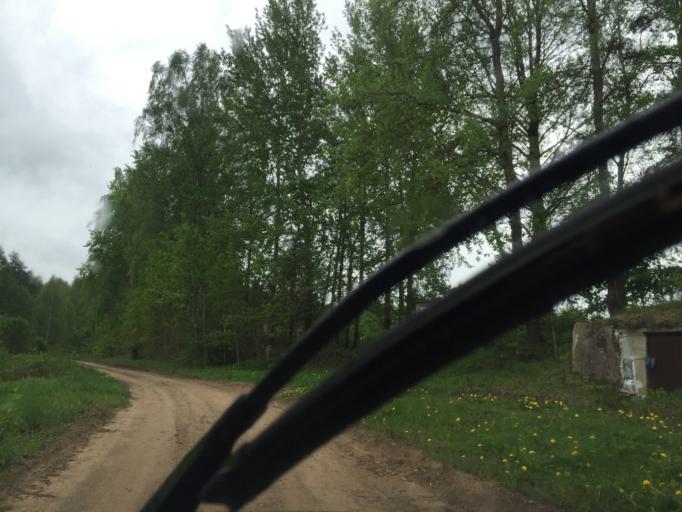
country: LV
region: Kegums
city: Kegums
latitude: 56.7346
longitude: 24.7516
